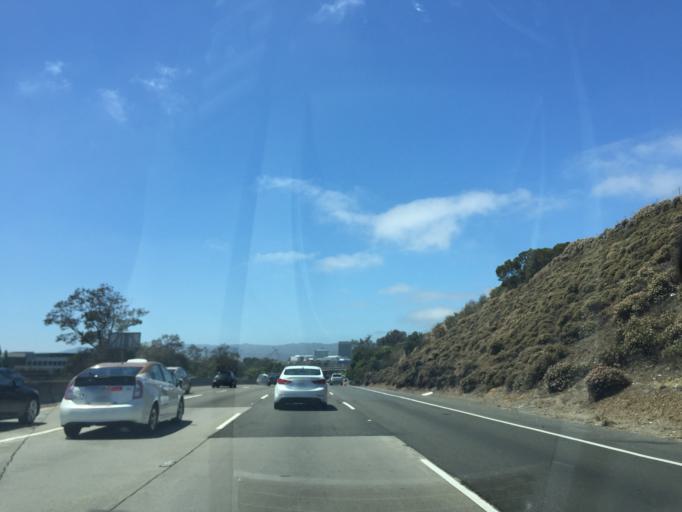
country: US
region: California
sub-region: San Mateo County
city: Brisbane
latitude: 37.6739
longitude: -122.3900
